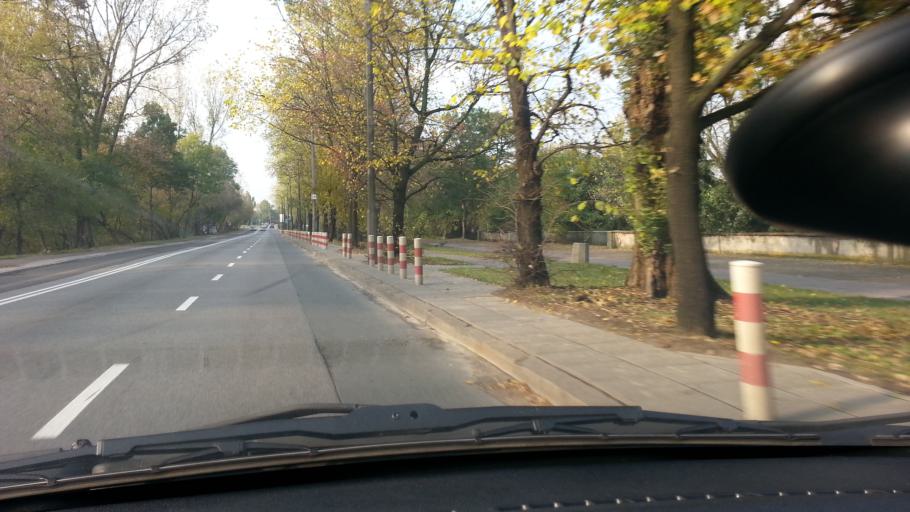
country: PL
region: Masovian Voivodeship
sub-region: Warszawa
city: Praga Polnoc
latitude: 52.2583
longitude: 21.0181
